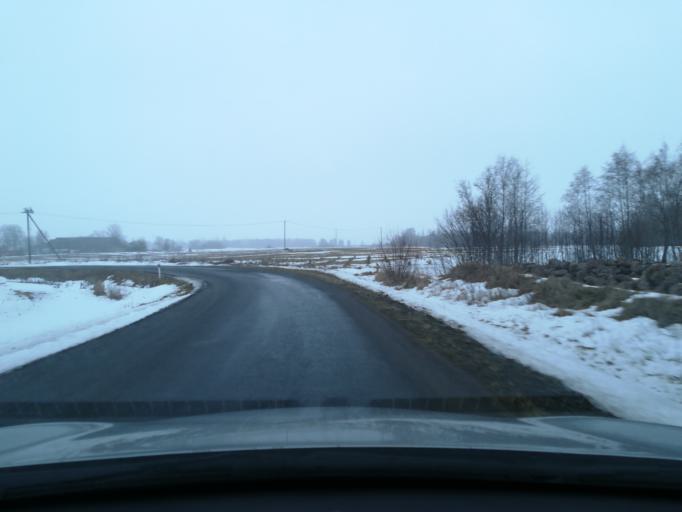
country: EE
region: Harju
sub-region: Raasiku vald
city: Raasiku
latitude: 59.3544
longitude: 25.2067
